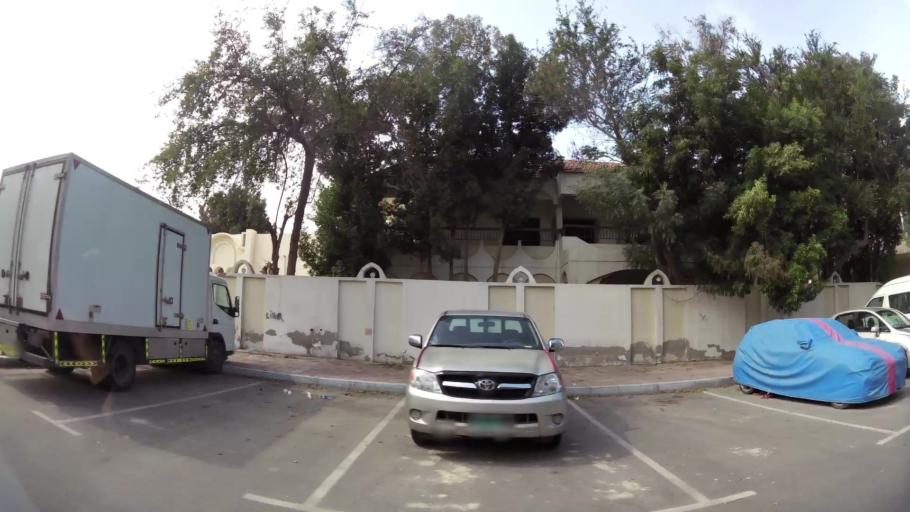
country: AE
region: Abu Dhabi
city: Abu Dhabi
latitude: 24.4411
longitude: 54.3697
